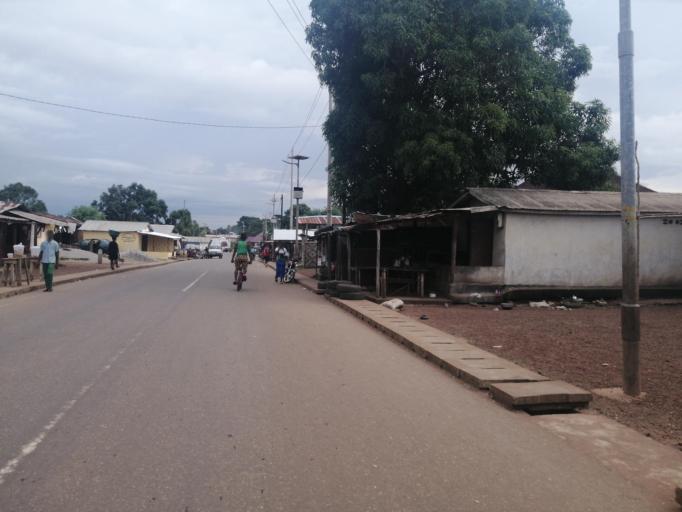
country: SL
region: Northern Province
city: Port Loko
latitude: 8.7729
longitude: -12.7884
